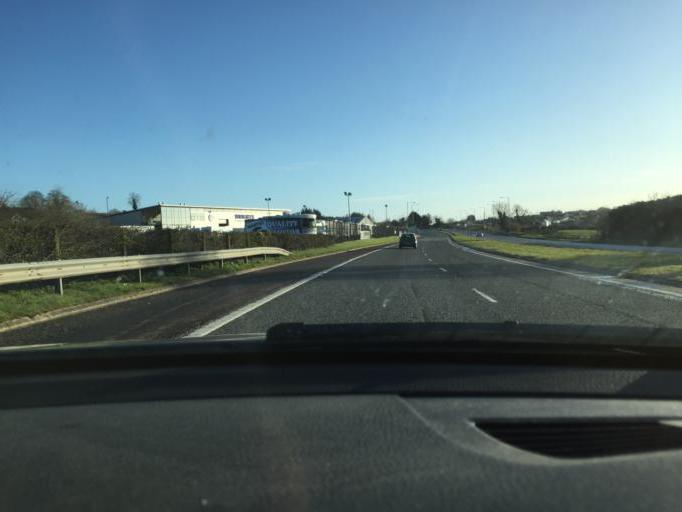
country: GB
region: Northern Ireland
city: Moira
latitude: 54.4030
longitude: -6.1712
